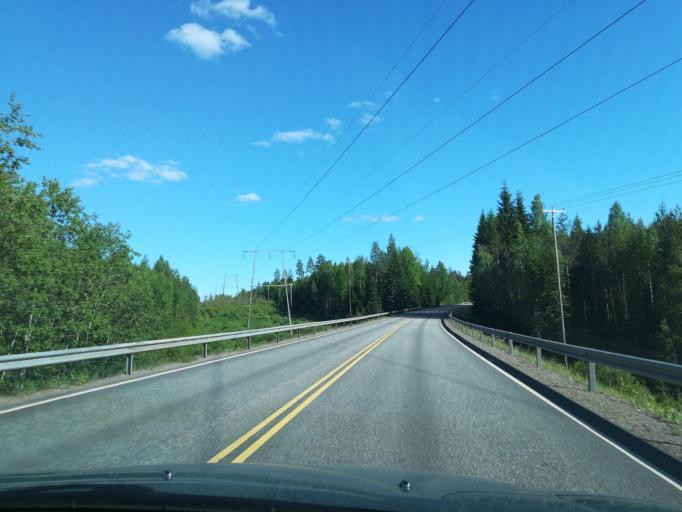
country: FI
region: South Karelia
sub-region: Imatra
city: Ruokolahti
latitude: 61.3871
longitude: 28.6512
